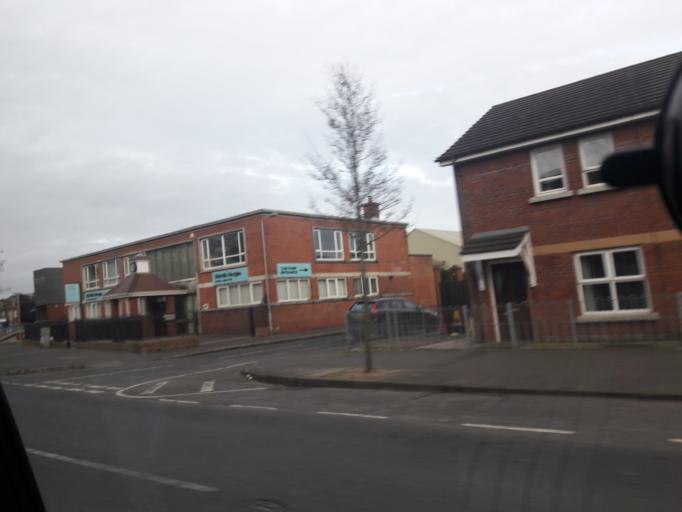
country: GB
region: Northern Ireland
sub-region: City of Belfast
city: Belfast
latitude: 54.6214
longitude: -5.9235
